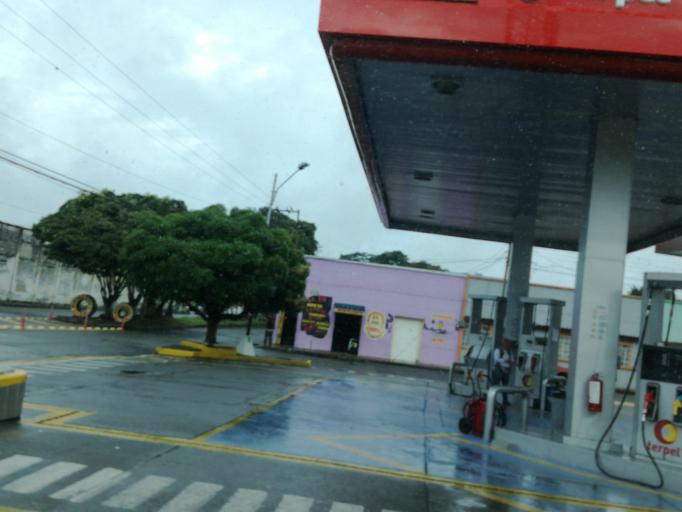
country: CO
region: Valle del Cauca
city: Palmira
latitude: 3.5218
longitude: -76.3035
